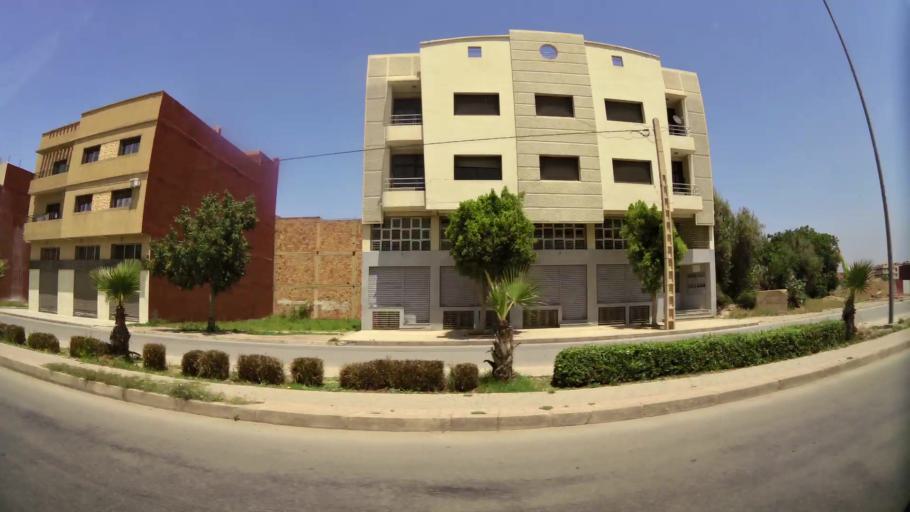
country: MA
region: Oriental
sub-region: Oujda-Angad
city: Oujda
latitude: 34.6922
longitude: -1.8969
